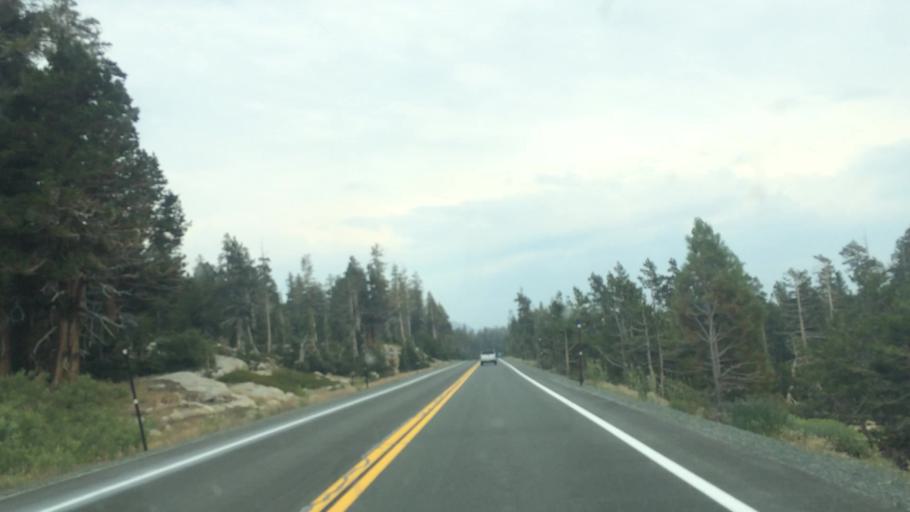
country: US
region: California
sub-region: El Dorado County
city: South Lake Tahoe
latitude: 38.6344
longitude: -120.1544
